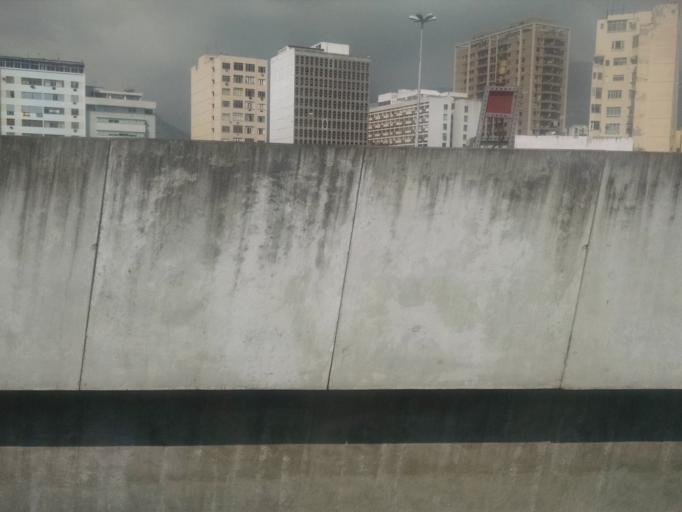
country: BR
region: Rio de Janeiro
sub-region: Rio De Janeiro
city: Rio de Janeiro
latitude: -22.9102
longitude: -43.2150
